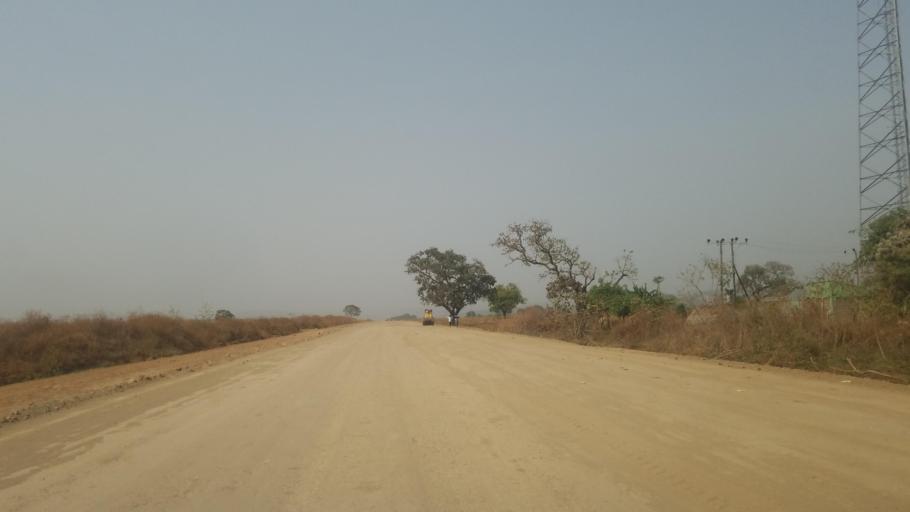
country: ET
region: Amhara
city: Bure
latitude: 10.8962
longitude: 36.4610
